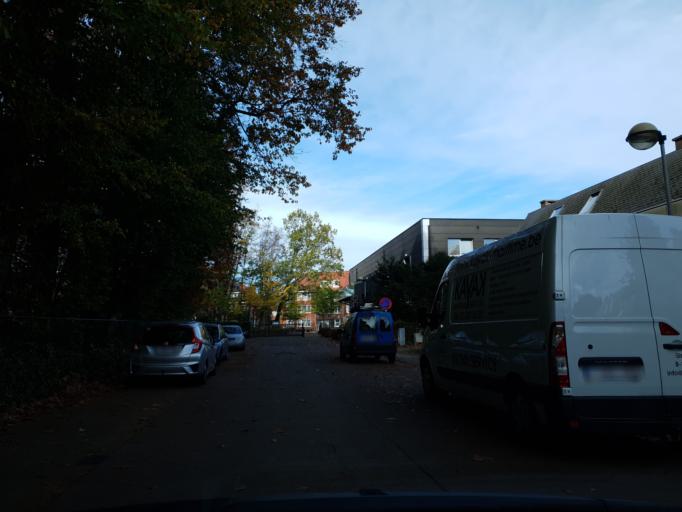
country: BE
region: Flanders
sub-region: Provincie Antwerpen
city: Schoten
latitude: 51.2440
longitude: 4.4667
